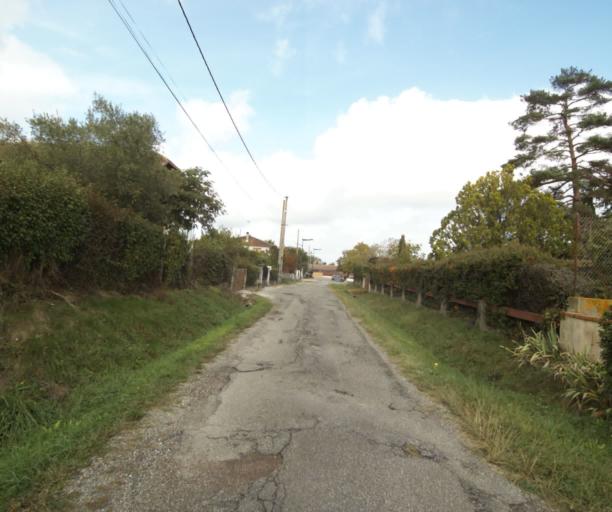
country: FR
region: Midi-Pyrenees
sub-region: Departement du Tarn-et-Garonne
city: Finhan
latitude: 43.8985
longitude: 1.1330
